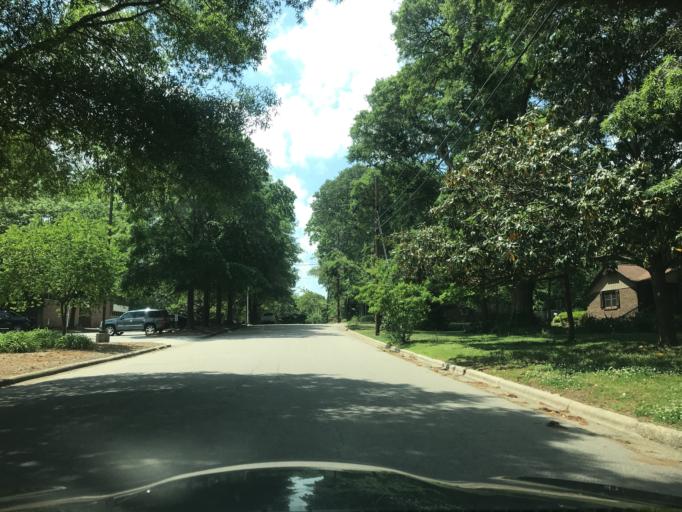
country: US
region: North Carolina
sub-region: Wake County
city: Raleigh
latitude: 35.7762
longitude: -78.6173
